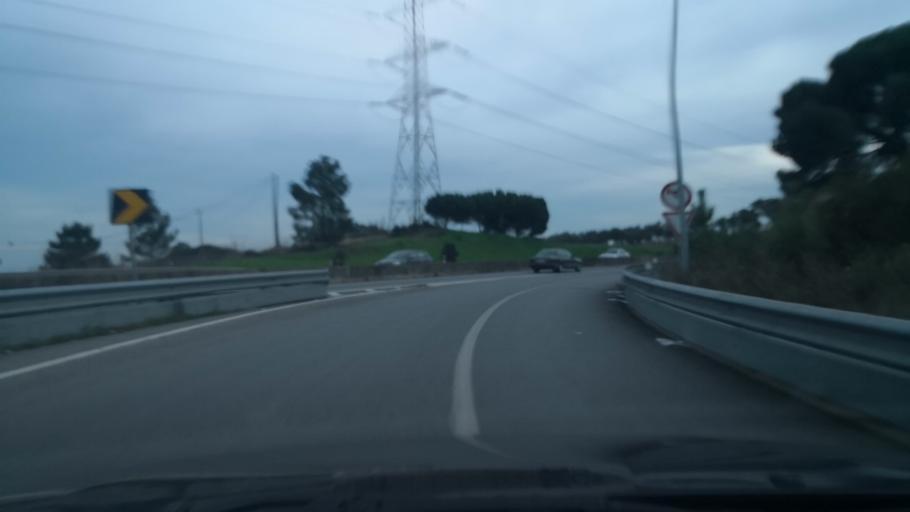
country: PT
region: Setubal
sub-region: Setubal
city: Setubal
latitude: 38.5364
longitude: -8.8427
